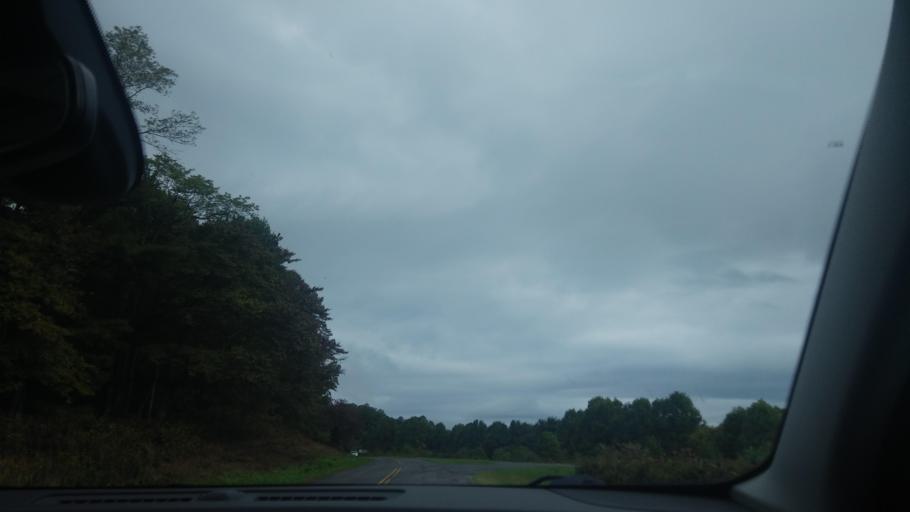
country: US
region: North Carolina
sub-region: Surry County
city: Flat Rock
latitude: 36.6418
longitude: -80.5357
